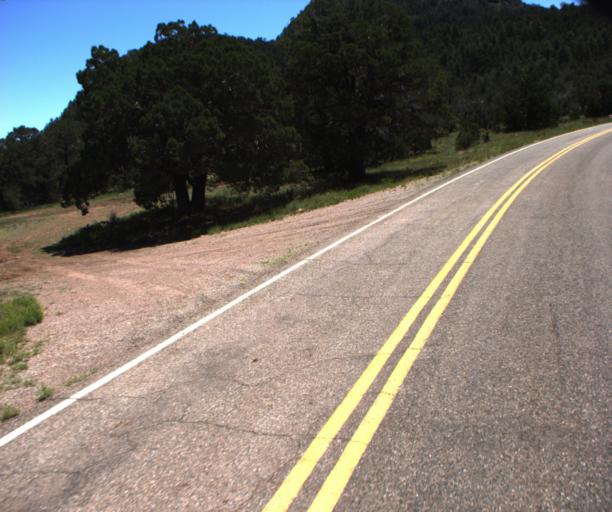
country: US
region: Arizona
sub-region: Greenlee County
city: Morenci
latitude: 33.3775
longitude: -109.3300
